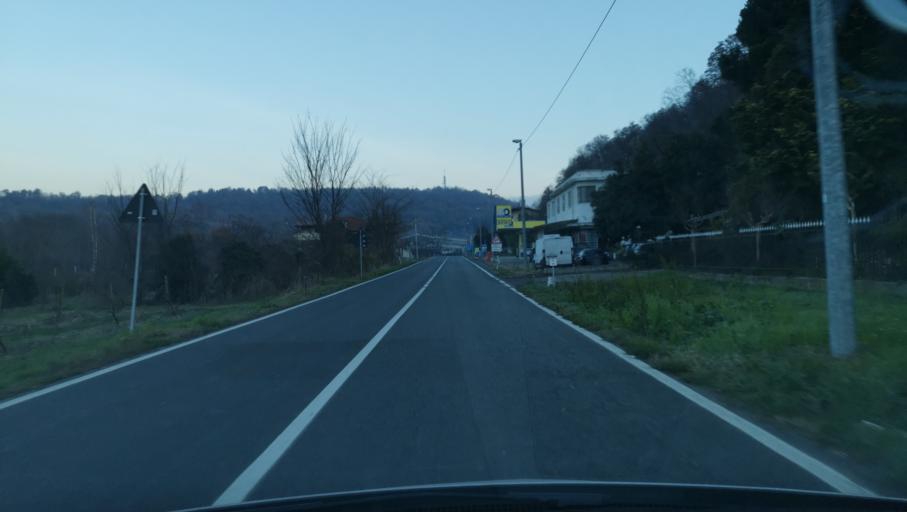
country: IT
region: Piedmont
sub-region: Provincia di Torino
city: Barone Canavese
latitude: 45.3218
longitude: 7.8785
